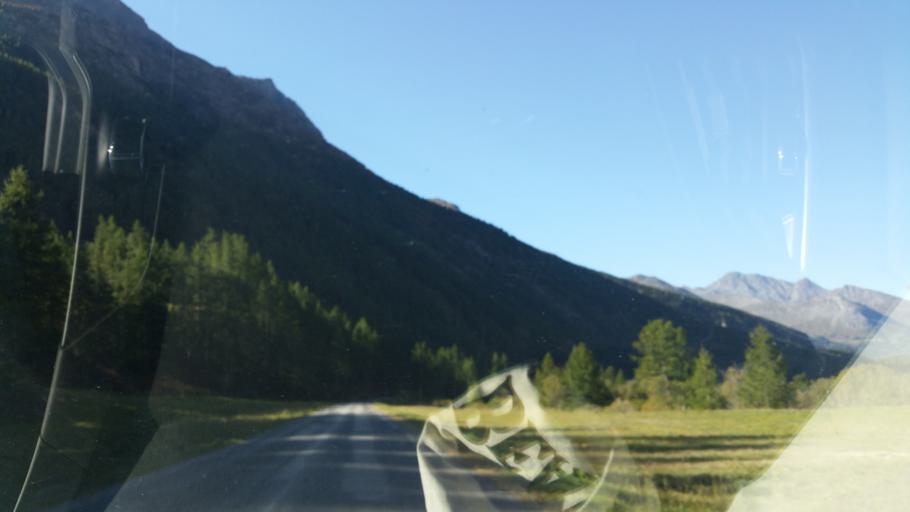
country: IT
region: Piedmont
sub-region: Provincia di Torino
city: Moncenisio
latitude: 45.3140
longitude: 6.9824
